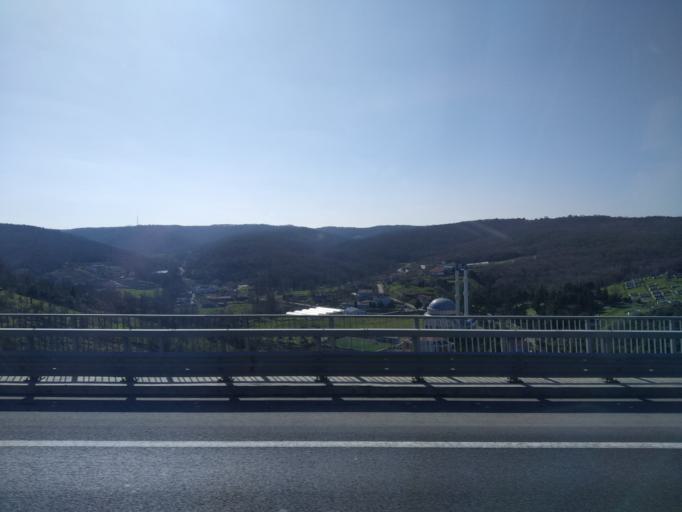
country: TR
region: Istanbul
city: Mahmut Sevket Pasa
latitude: 41.1807
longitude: 29.2343
